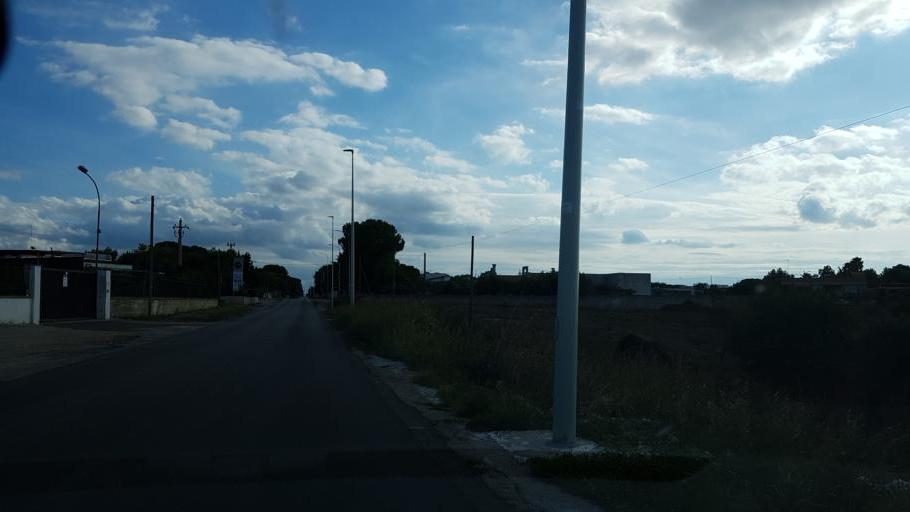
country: IT
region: Apulia
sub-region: Provincia di Lecce
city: Nardo
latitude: 40.1473
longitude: 18.0184
